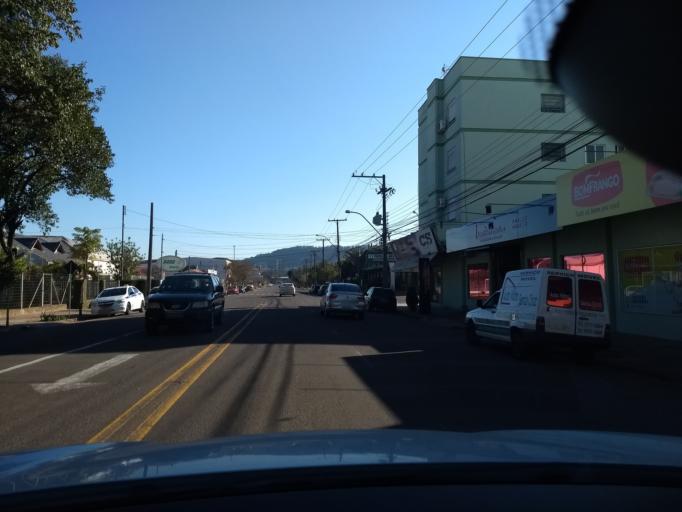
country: BR
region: Rio Grande do Sul
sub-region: Santa Cruz Do Sul
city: Santa Cruz do Sul
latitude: -29.7116
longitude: -52.4356
